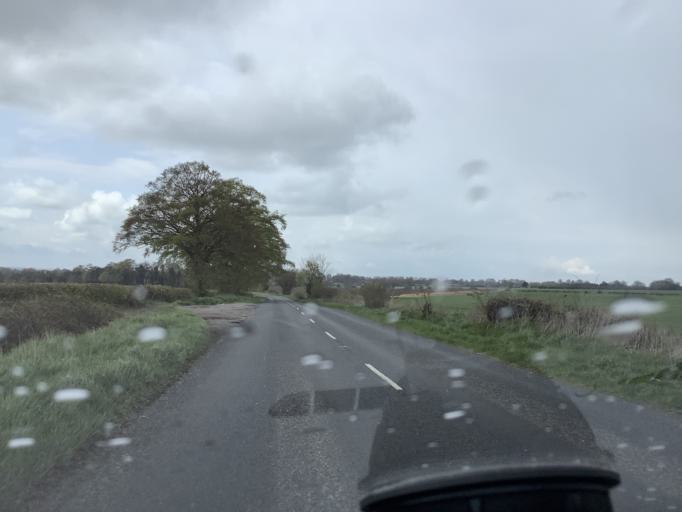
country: GB
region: England
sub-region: Borough of Swindon
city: Wroughton
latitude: 51.4990
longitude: -1.8320
